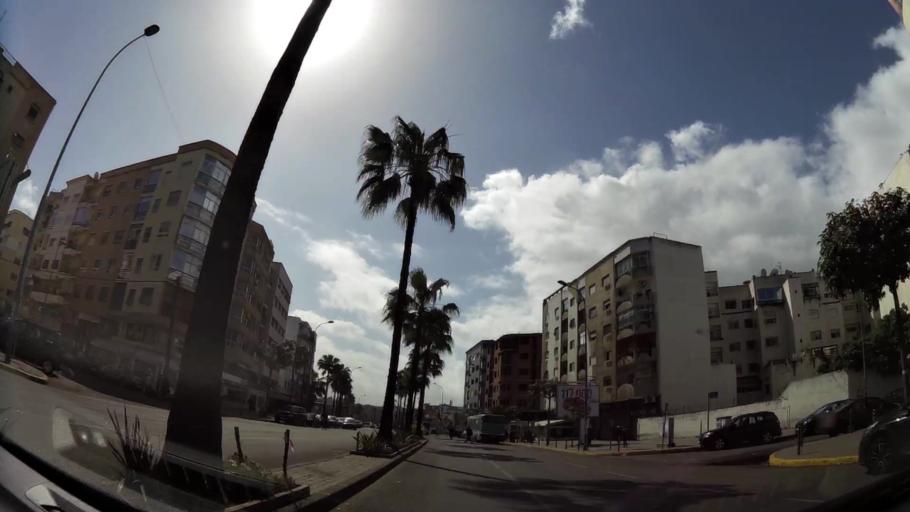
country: MA
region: Grand Casablanca
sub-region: Casablanca
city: Casablanca
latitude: 33.5707
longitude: -7.6129
